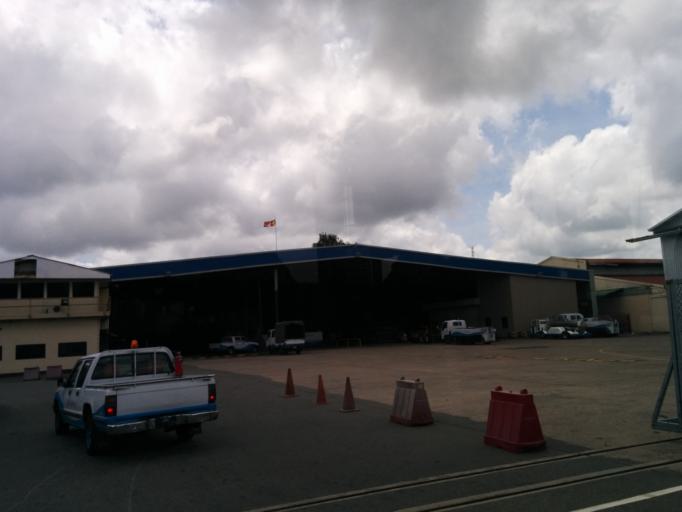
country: LK
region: Western
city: Katunayaka
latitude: 7.1776
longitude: 79.8877
